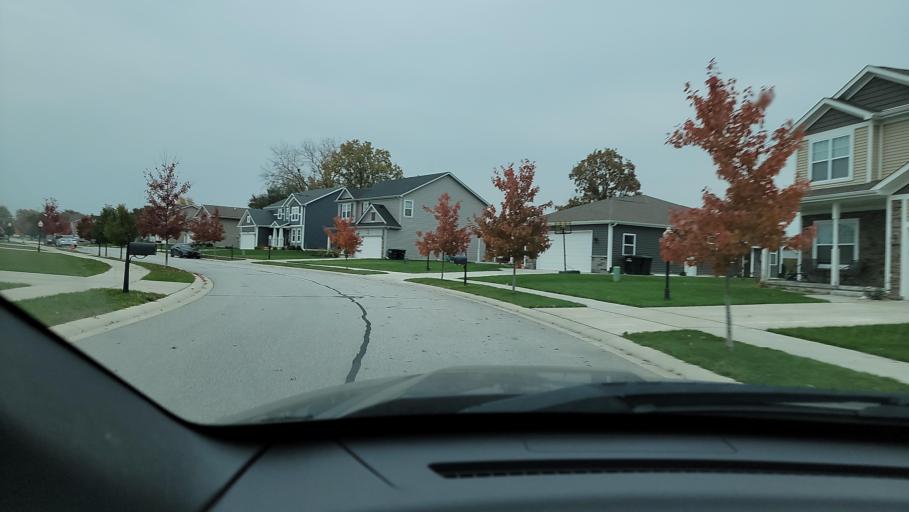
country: US
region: Indiana
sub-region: Porter County
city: Portage
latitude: 41.5657
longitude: -87.1697
